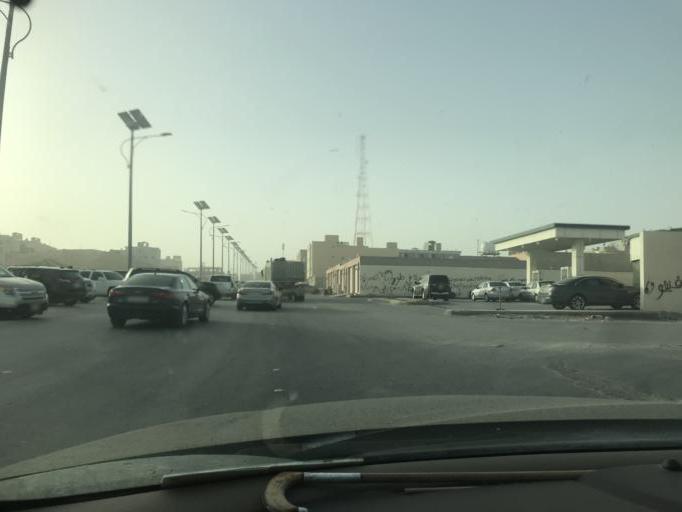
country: SA
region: Ar Riyad
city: Riyadh
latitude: 24.8426
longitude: 46.6657
